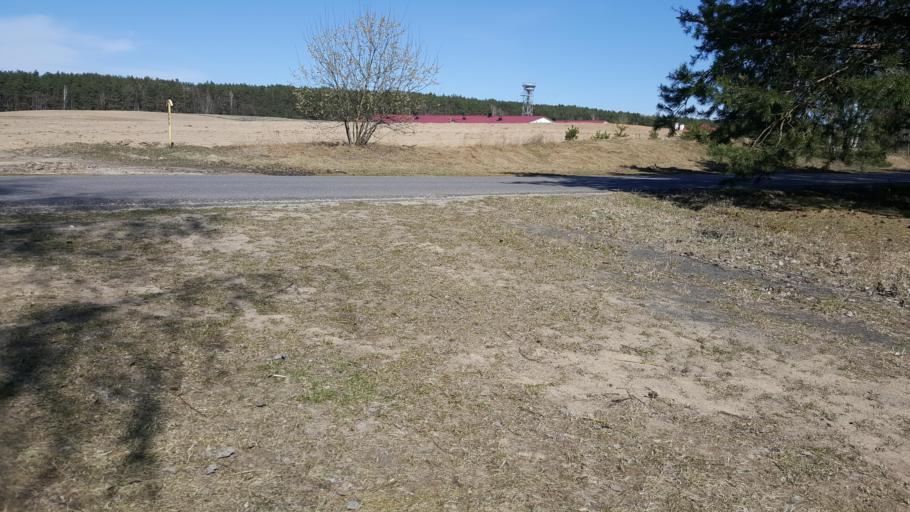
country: BY
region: Brest
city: Charnawchytsy
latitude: 52.2891
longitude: 23.7784
